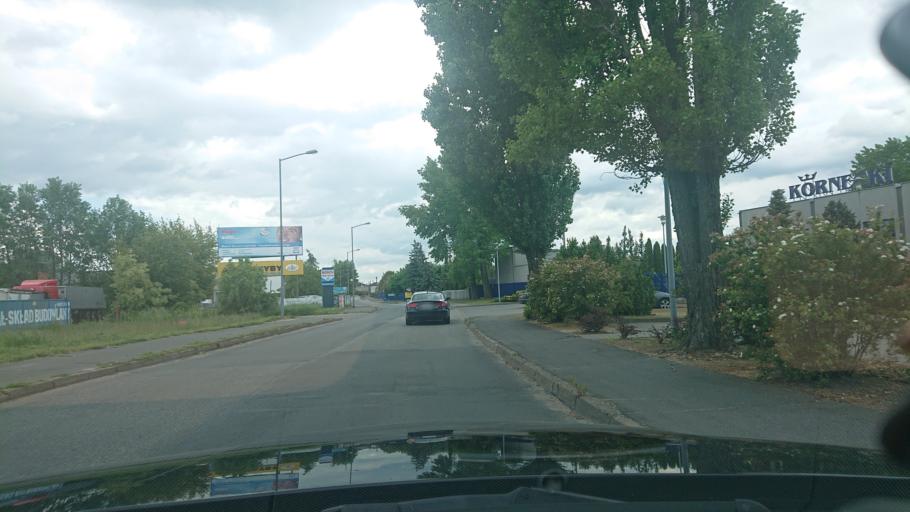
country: PL
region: Greater Poland Voivodeship
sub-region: Powiat gnieznienski
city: Gniezno
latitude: 52.5394
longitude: 17.6292
